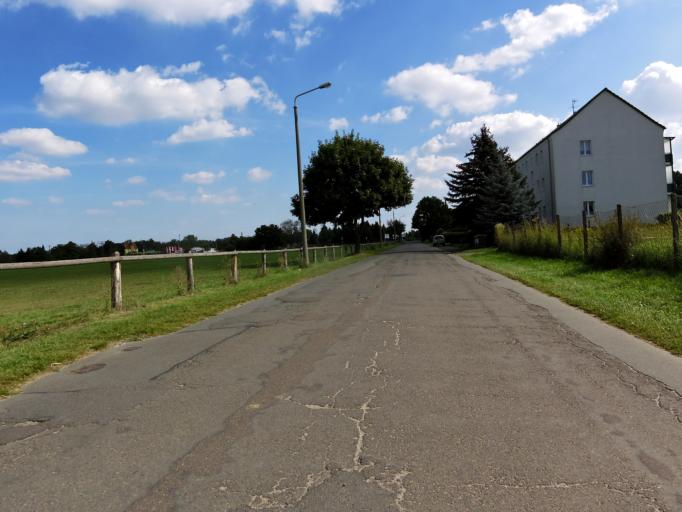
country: DE
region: Saxony
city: Leipzig
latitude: 51.3691
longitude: 12.4222
